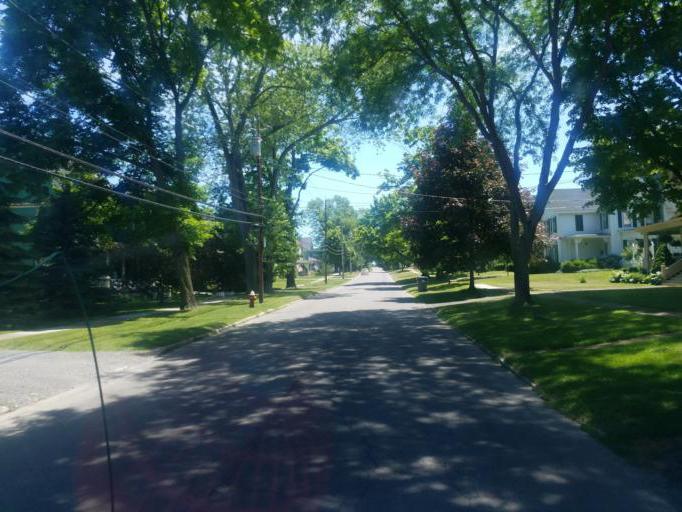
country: US
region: New York
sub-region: Yates County
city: Penn Yan
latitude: 42.6560
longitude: -77.0466
